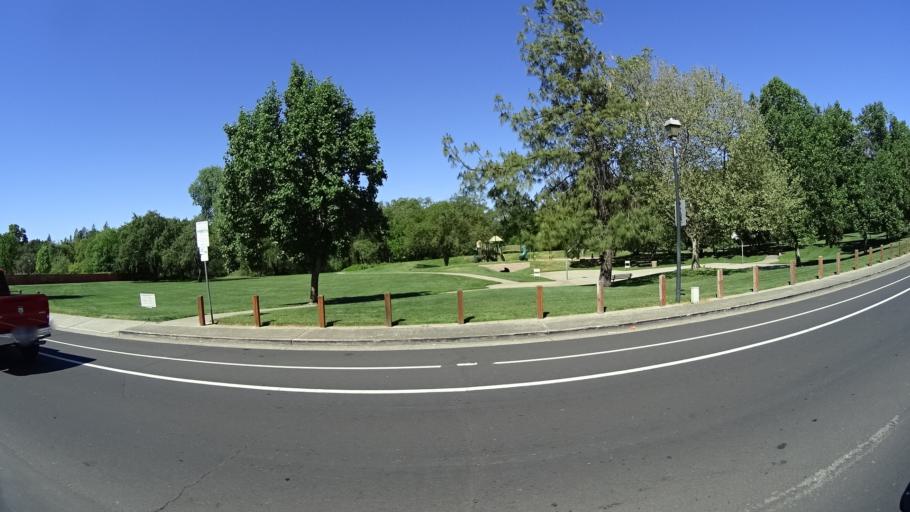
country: US
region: California
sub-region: Placer County
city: Rocklin
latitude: 38.7945
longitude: -121.2226
